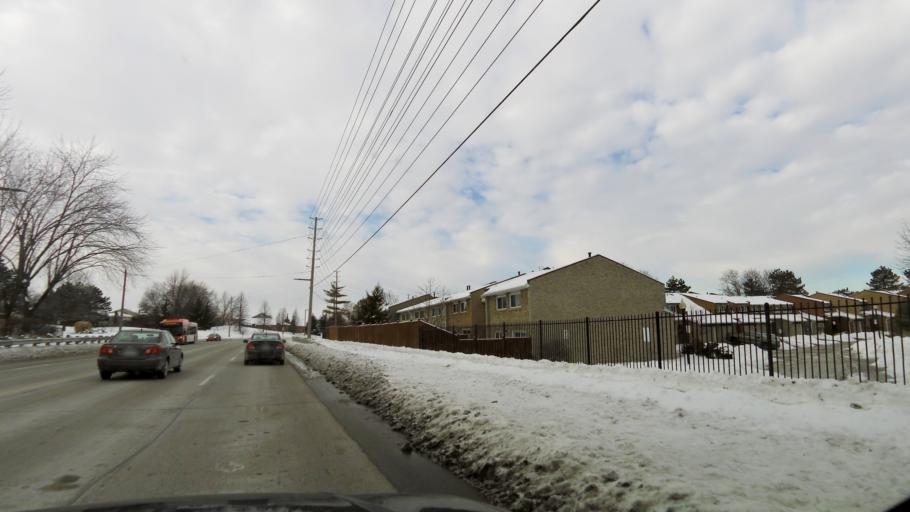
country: CA
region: Ontario
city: Mississauga
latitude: 43.5358
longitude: -79.6832
